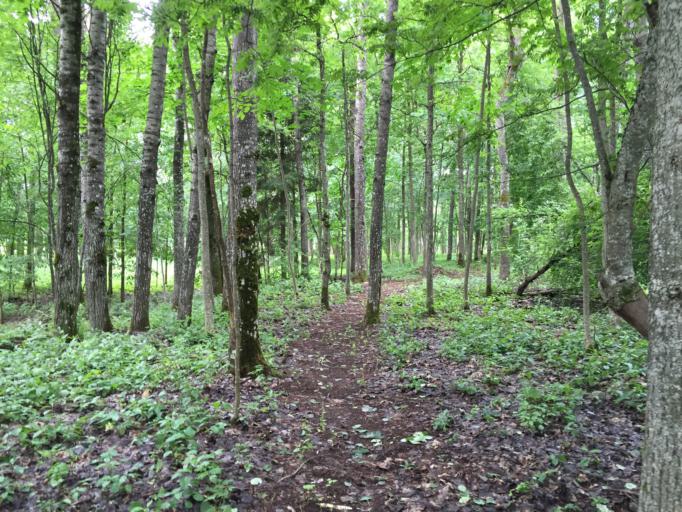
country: LV
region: Lecava
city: Iecava
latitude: 56.5759
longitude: 24.1133
